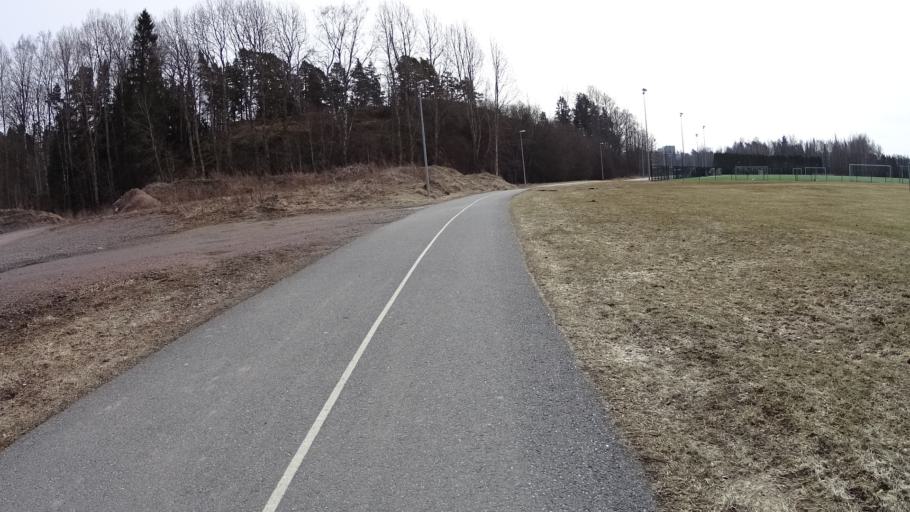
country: FI
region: Uusimaa
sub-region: Helsinki
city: Kilo
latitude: 60.2273
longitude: 24.7939
